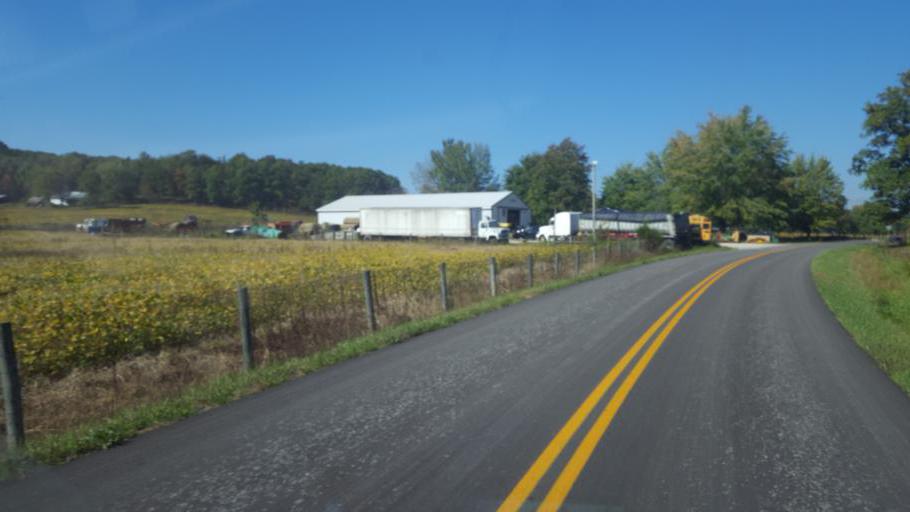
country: US
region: Kentucky
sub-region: Fleming County
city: Flemingsburg
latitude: 38.4483
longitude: -83.5831
